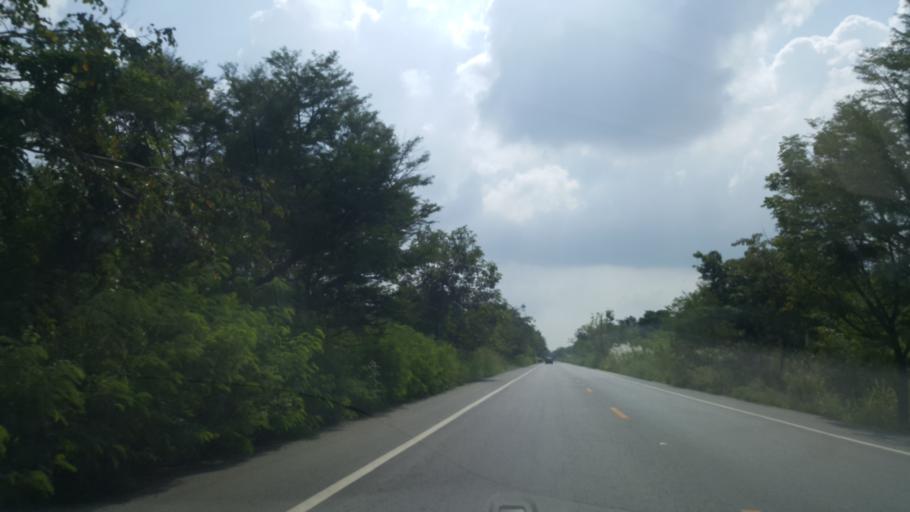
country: TH
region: Chon Buri
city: Sattahip
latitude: 12.7308
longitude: 100.9551
